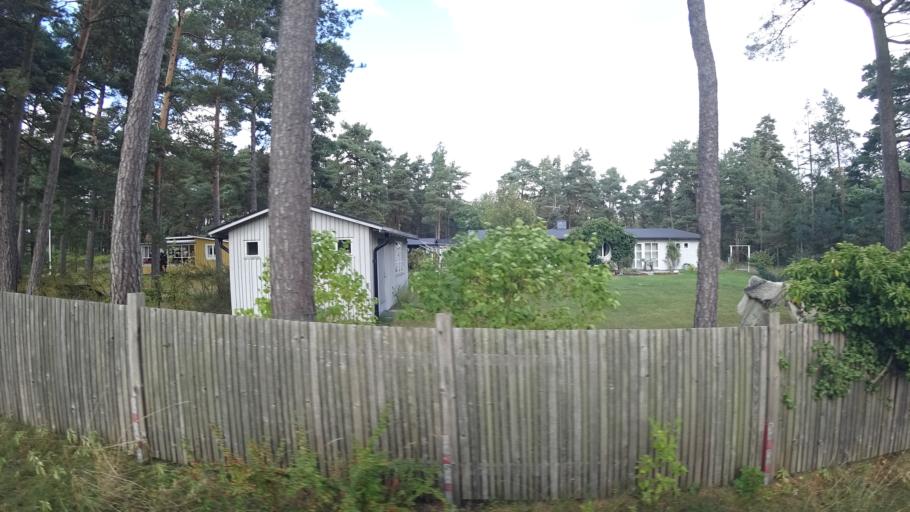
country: SE
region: Skane
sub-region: Kristianstads Kommun
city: Ahus
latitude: 55.9349
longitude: 14.3106
